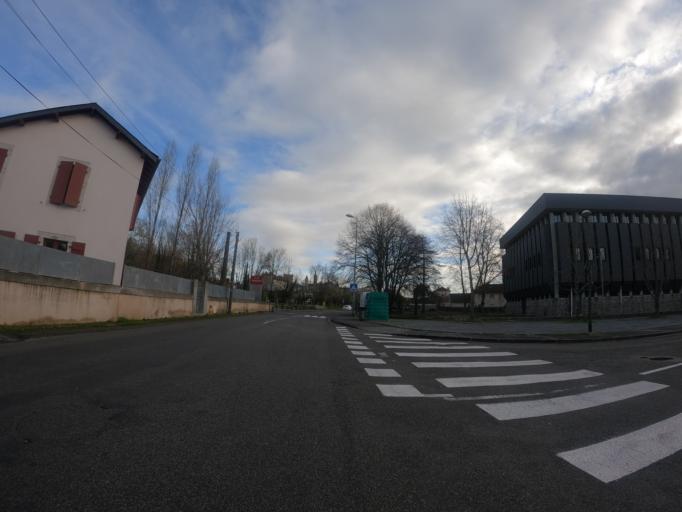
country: FR
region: Aquitaine
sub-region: Departement des Pyrenees-Atlantiques
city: Jurancon
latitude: 43.2933
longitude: -0.3827
